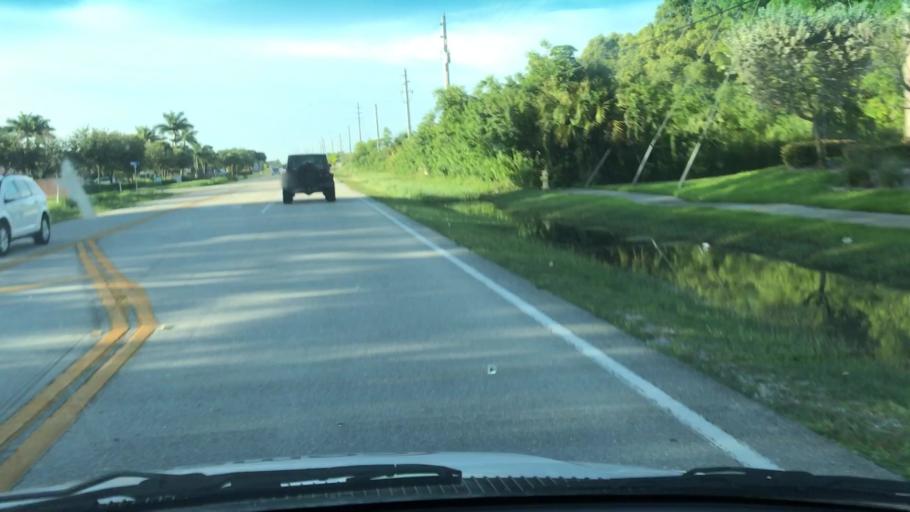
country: US
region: Florida
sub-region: Lee County
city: Villas
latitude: 26.5419
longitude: -81.8470
